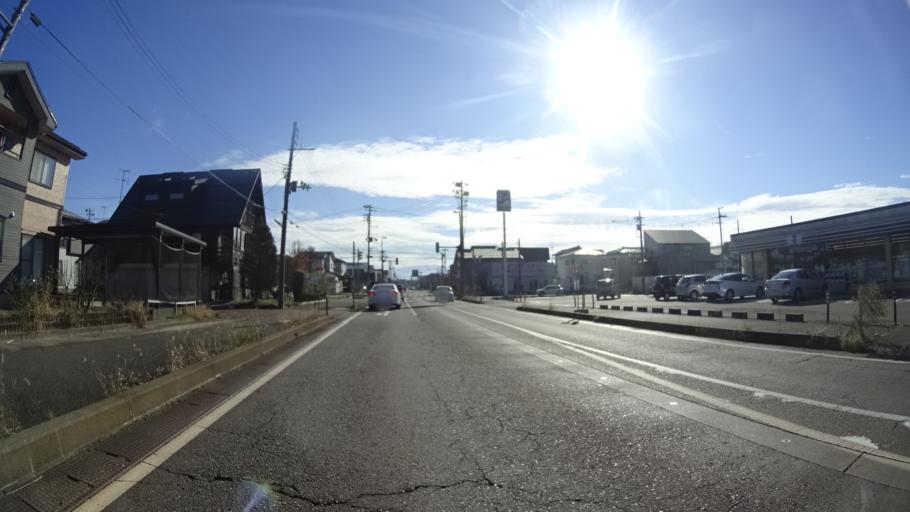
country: JP
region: Niigata
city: Mitsuke
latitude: 37.5442
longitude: 138.8851
